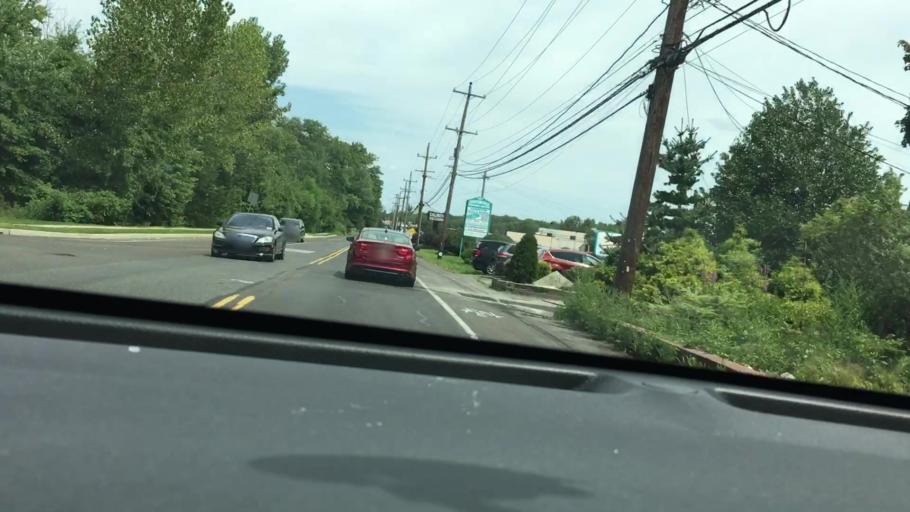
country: US
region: Pennsylvania
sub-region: Bucks County
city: Feasterville
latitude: 40.1346
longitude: -75.0021
